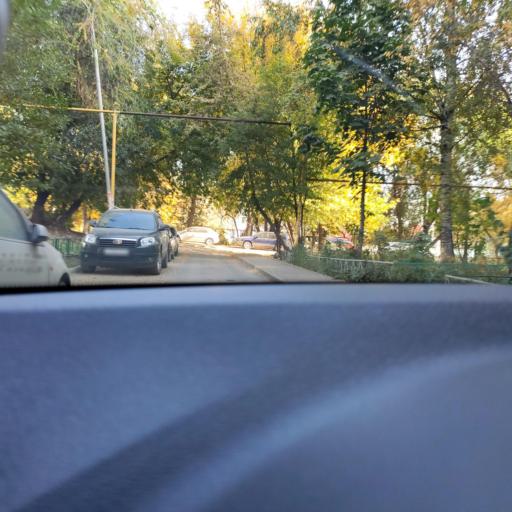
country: RU
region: Samara
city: Samara
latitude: 53.2423
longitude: 50.2578
